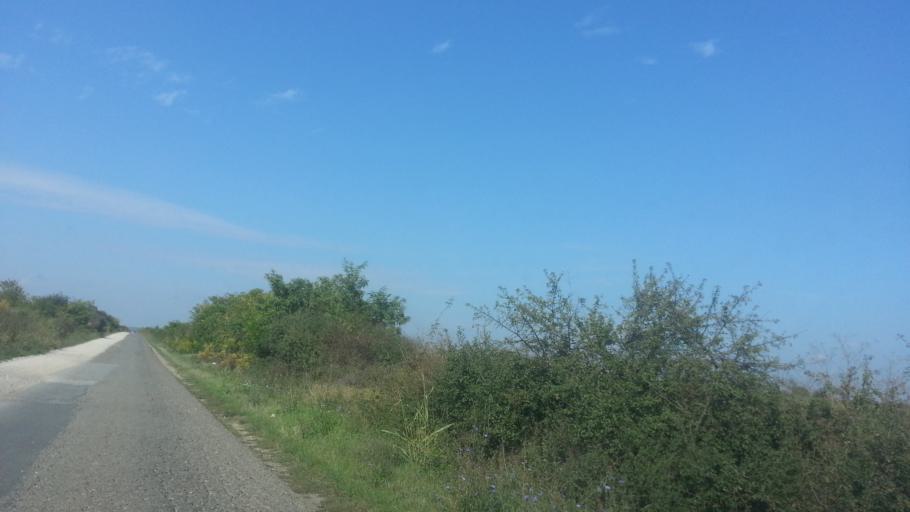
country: RS
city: Surduk
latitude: 45.1006
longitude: 20.2891
